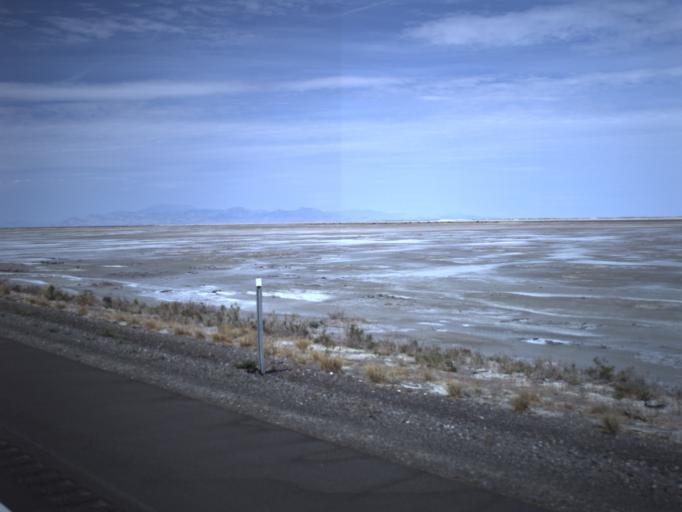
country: US
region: Utah
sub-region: Tooele County
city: Wendover
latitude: 40.7281
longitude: -113.3017
